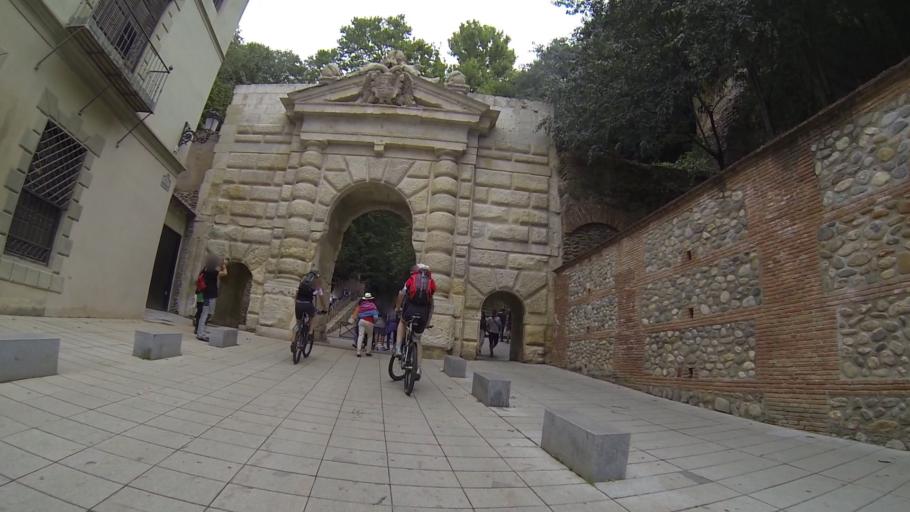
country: ES
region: Andalusia
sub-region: Provincia de Granada
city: Granada
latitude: 37.1761
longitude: -3.5932
